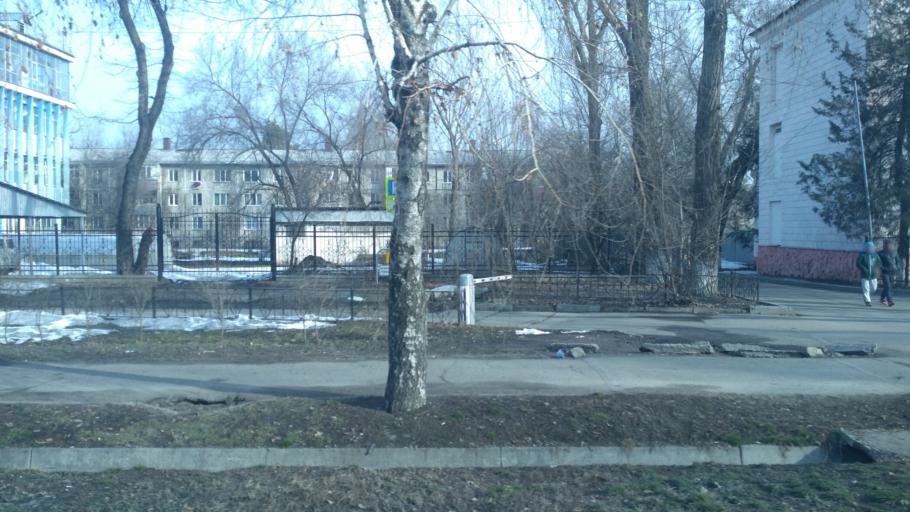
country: KZ
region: Almaty Qalasy
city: Almaty
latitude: 43.2268
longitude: 76.9170
